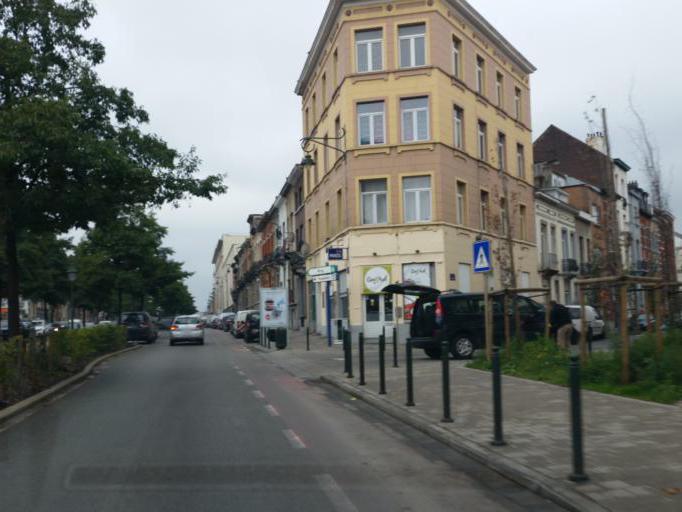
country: BE
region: Brussels Capital
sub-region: Bruxelles-Capitale
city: Brussels
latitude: 50.8241
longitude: 4.3240
